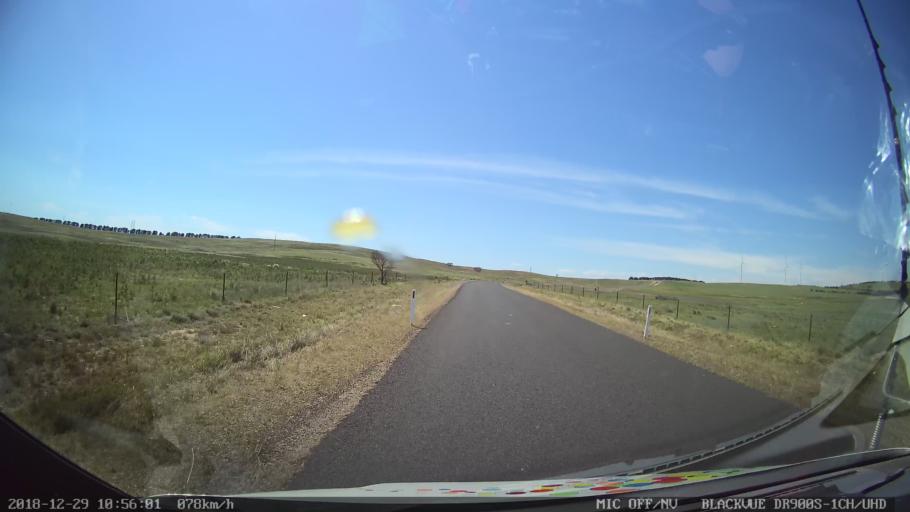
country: AU
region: New South Wales
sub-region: Palerang
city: Bungendore
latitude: -35.1300
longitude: 149.5356
